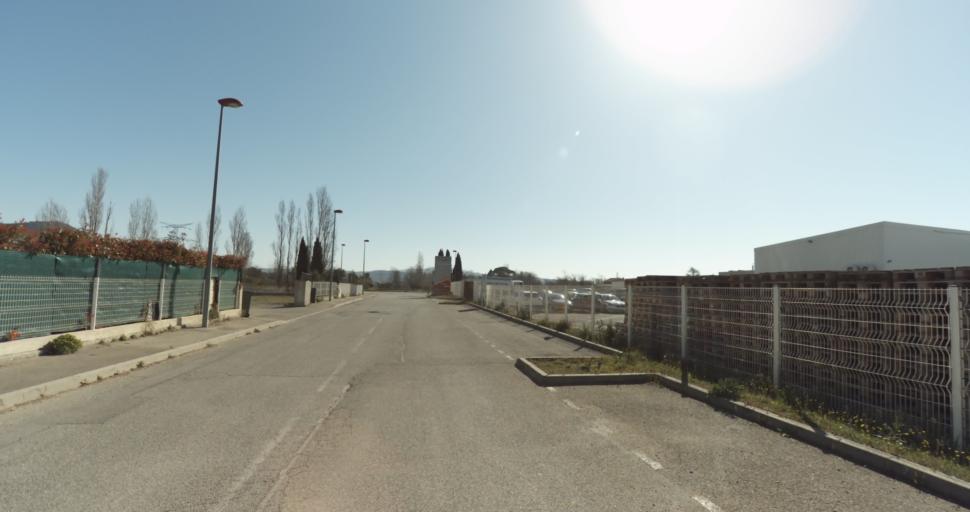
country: FR
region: Provence-Alpes-Cote d'Azur
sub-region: Departement des Bouches-du-Rhone
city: Peyrolles-en-Provence
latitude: 43.6561
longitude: 5.5789
